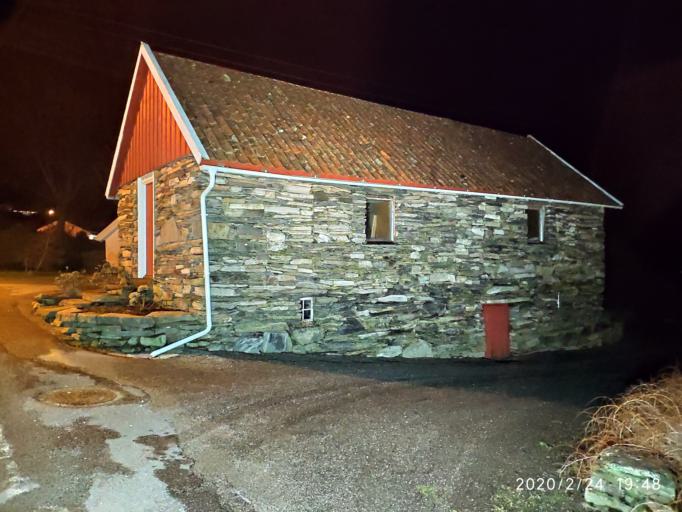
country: NO
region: Rogaland
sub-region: Finnoy
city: Judaberg
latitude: 59.3463
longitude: 5.8649
